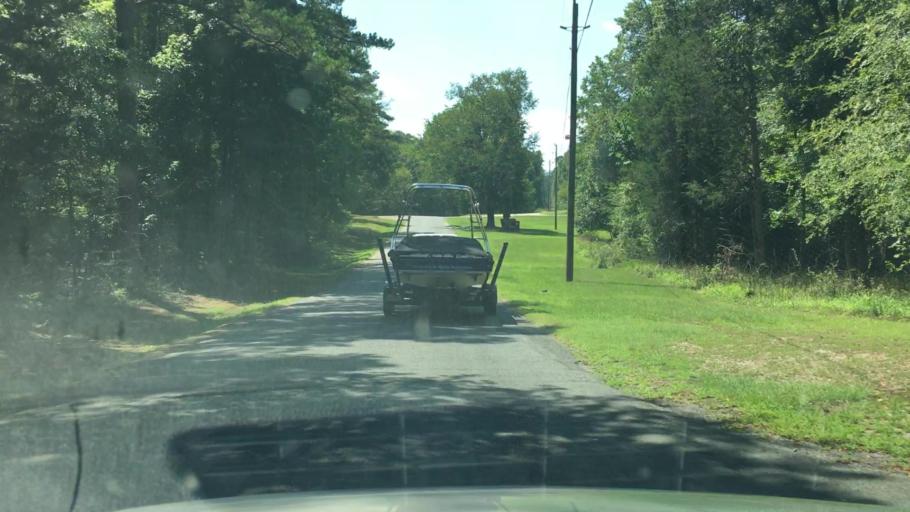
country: US
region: Arkansas
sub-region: Garland County
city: Piney
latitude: 34.5408
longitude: -93.3483
